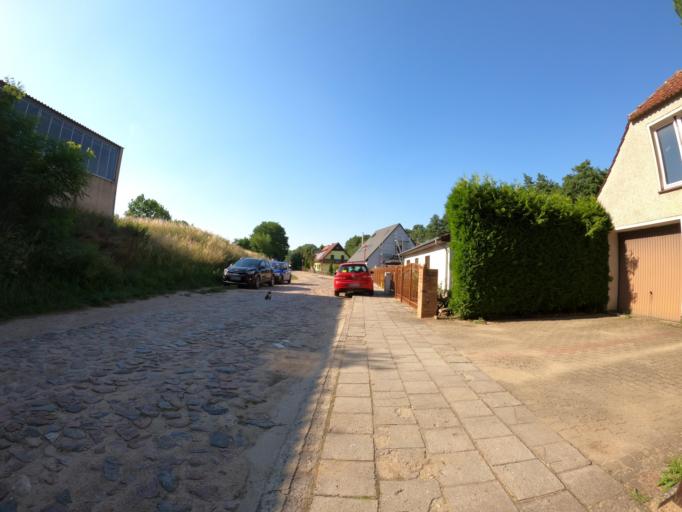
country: DE
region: Brandenburg
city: Gartz
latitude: 53.2117
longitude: 14.3796
